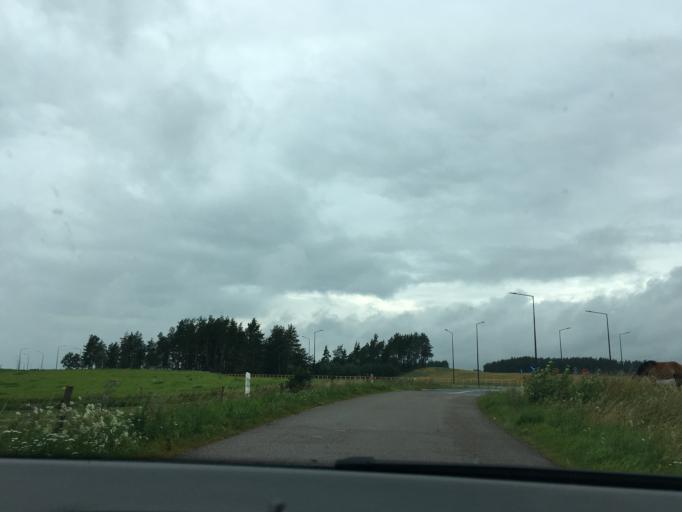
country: PL
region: Podlasie
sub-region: Powiat sejnenski
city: Krasnopol
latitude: 54.0978
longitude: 23.2209
